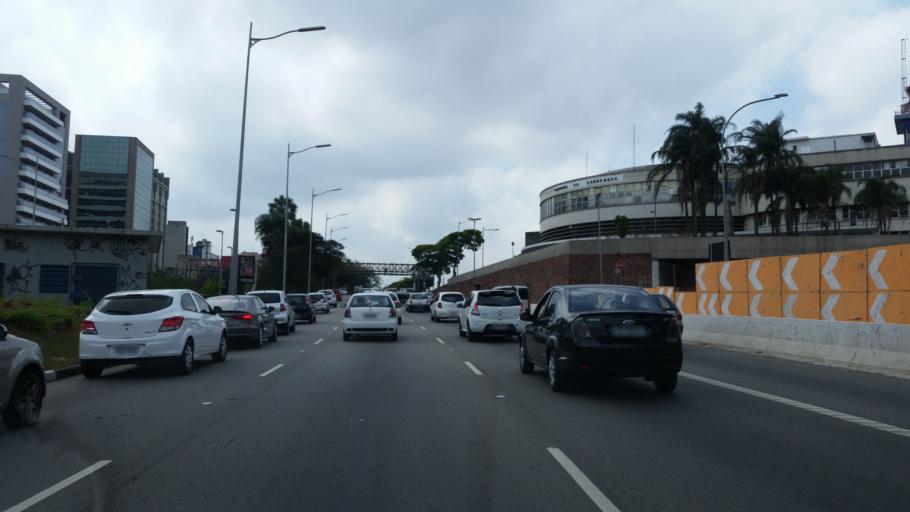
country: BR
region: Sao Paulo
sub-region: Diadema
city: Diadema
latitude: -23.6268
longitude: -46.6614
